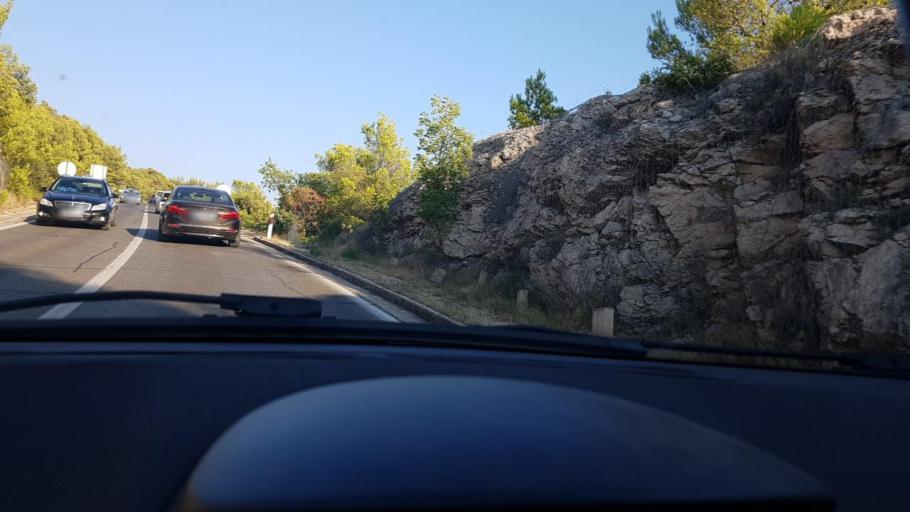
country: HR
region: Sibensko-Kniniska
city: Murter
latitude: 43.7985
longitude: 15.6135
